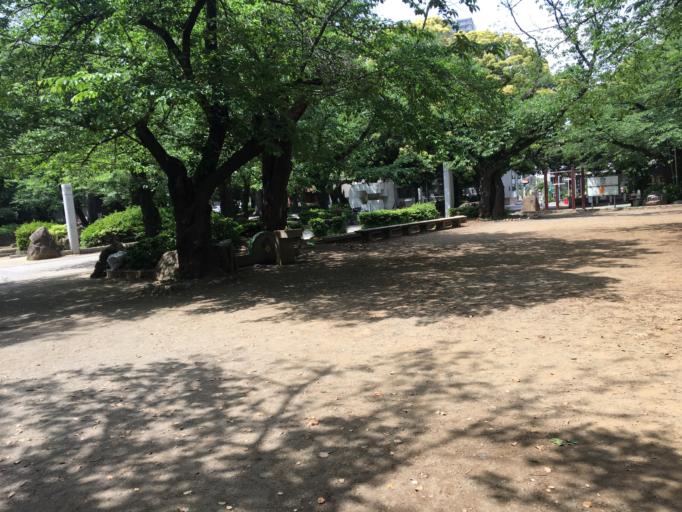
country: JP
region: Saitama
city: Yono
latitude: 35.8533
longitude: 139.6570
